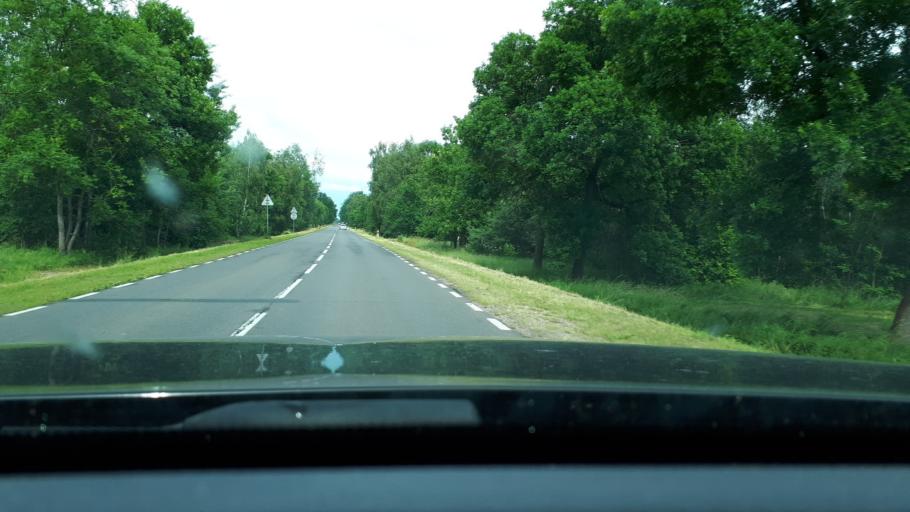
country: PL
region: Masovian Voivodeship
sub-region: Powiat sochaczewski
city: Paprotnia
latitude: 52.2662
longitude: 20.3828
